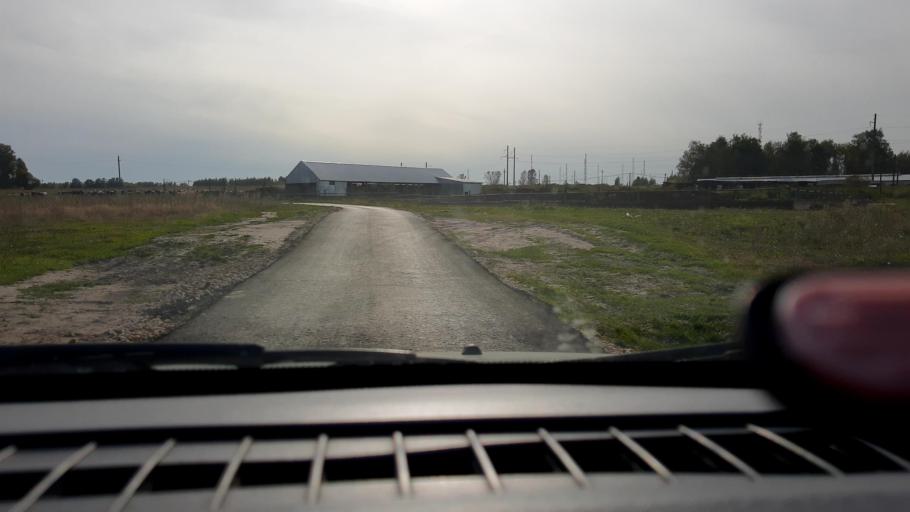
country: RU
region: Nizjnij Novgorod
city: Kstovo
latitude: 55.9964
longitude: 44.2224
